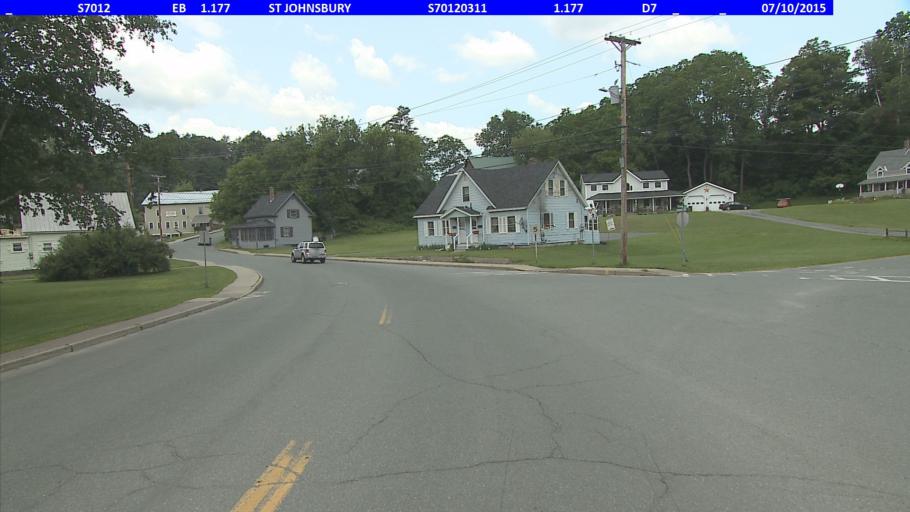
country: US
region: Vermont
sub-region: Caledonia County
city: St Johnsbury
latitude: 44.4249
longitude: -72.0111
